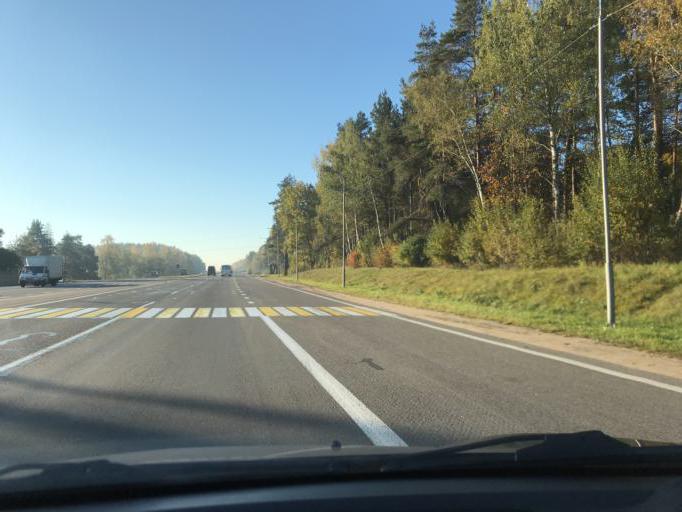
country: BY
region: Minsk
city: Luhavaya Slabada
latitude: 53.7743
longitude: 27.8268
